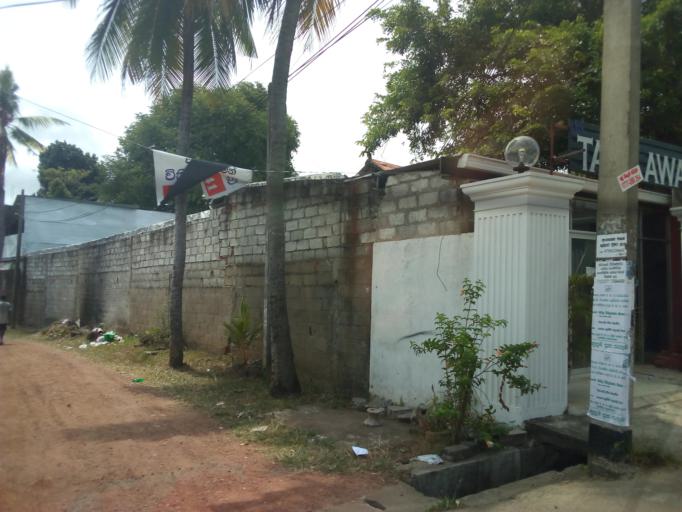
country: LK
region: Western
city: Galkissa
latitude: 6.8422
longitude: 79.8847
